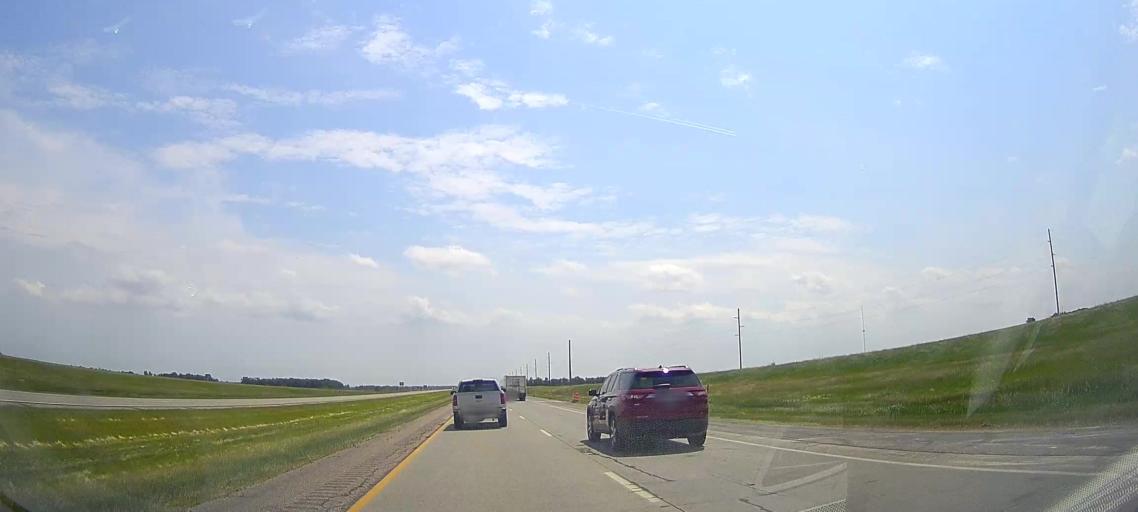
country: US
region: South Dakota
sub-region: Lincoln County
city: Tea
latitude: 43.3868
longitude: -96.7965
